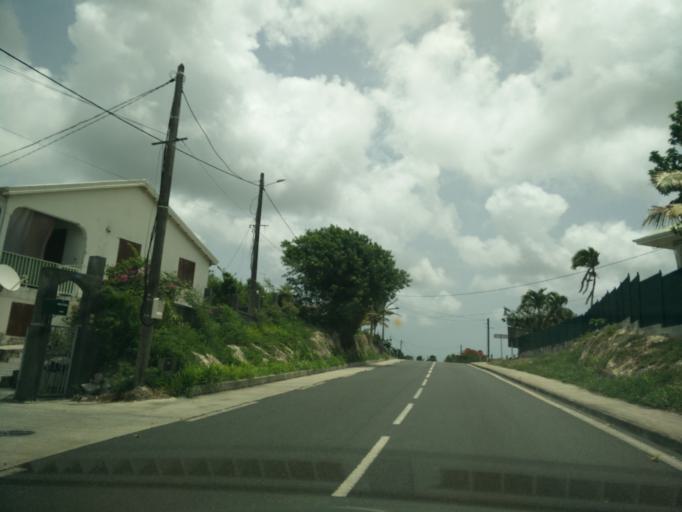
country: GP
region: Guadeloupe
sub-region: Guadeloupe
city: Port-Louis
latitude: 16.4207
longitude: -61.5254
